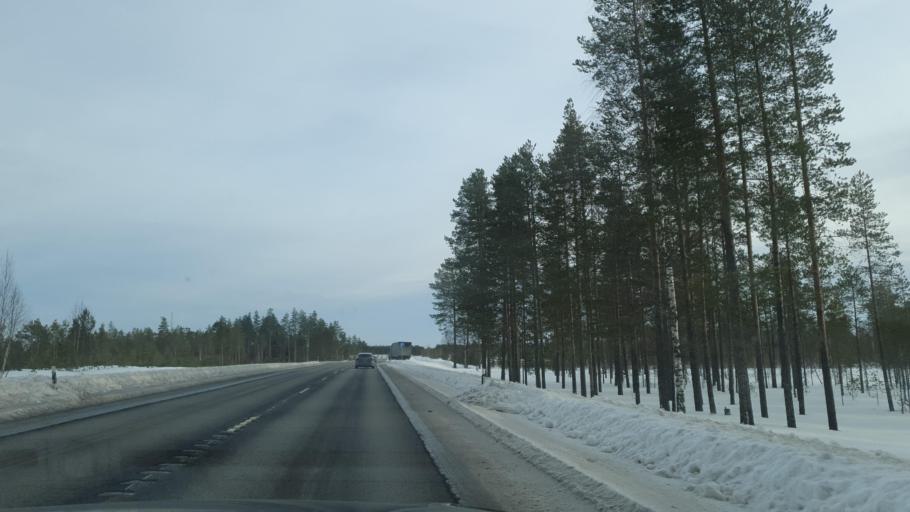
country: FI
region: Kainuu
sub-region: Kajaani
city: Vaala
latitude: 64.5797
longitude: 26.8353
